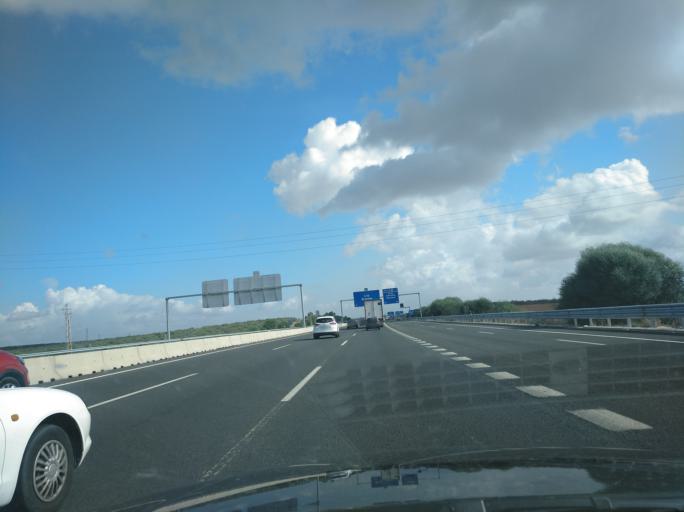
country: ES
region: Andalusia
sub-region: Provincia de Sevilla
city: Espartinas
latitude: 37.3641
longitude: -6.1281
